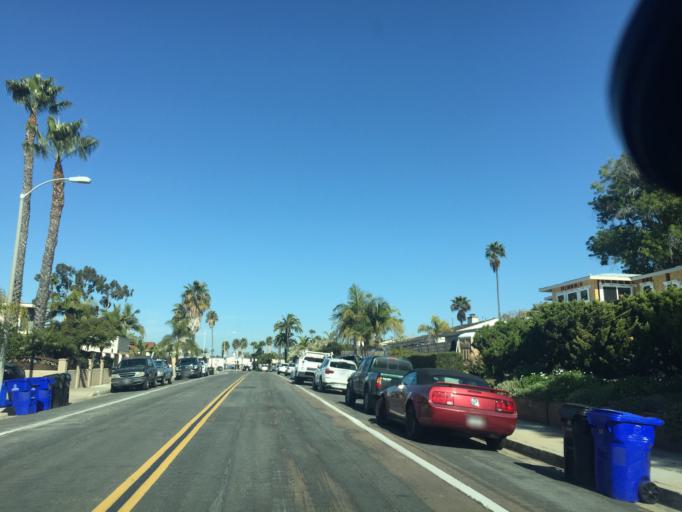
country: US
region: California
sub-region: San Diego County
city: San Diego
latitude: 32.7923
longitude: -117.1931
